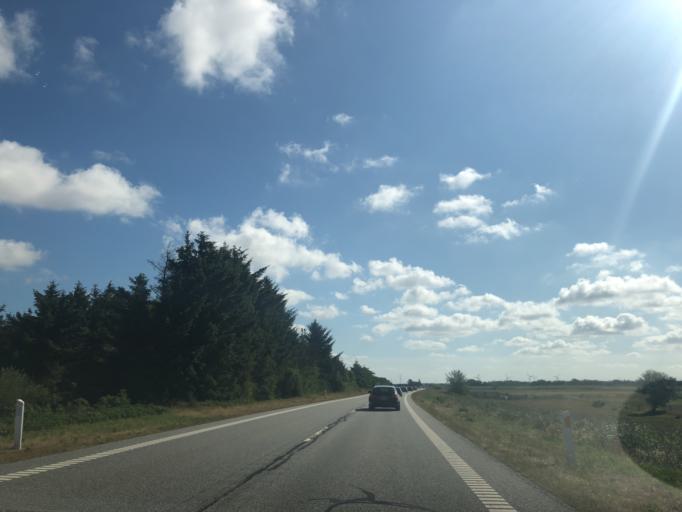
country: DK
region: North Denmark
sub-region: Jammerbugt Kommune
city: Fjerritslev
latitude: 57.0428
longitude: 9.1430
